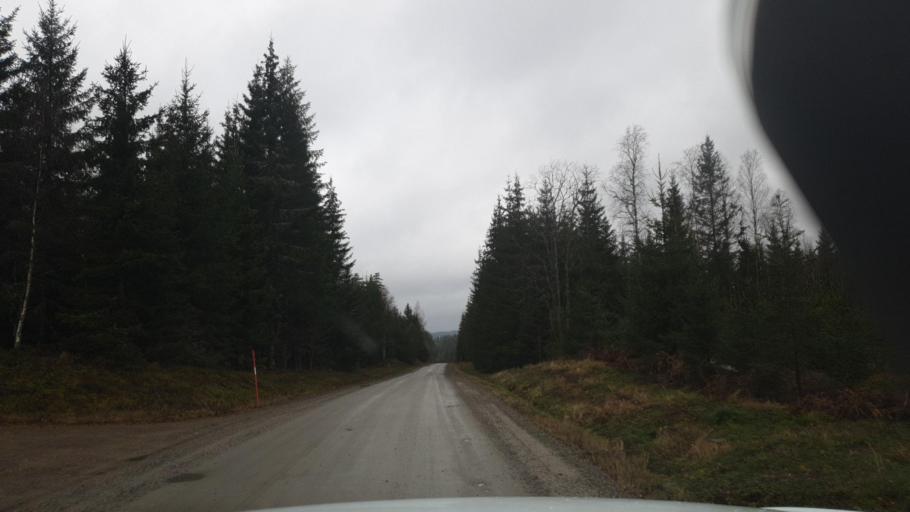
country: SE
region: Vaermland
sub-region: Arvika Kommun
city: Arvika
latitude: 59.8823
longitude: 12.6790
